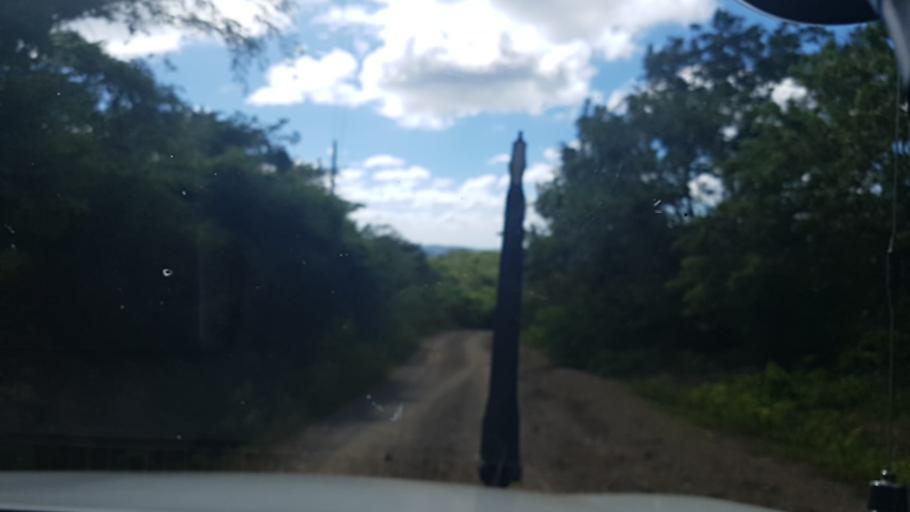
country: NI
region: Carazo
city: Santa Teresa
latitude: 11.6199
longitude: -86.1618
